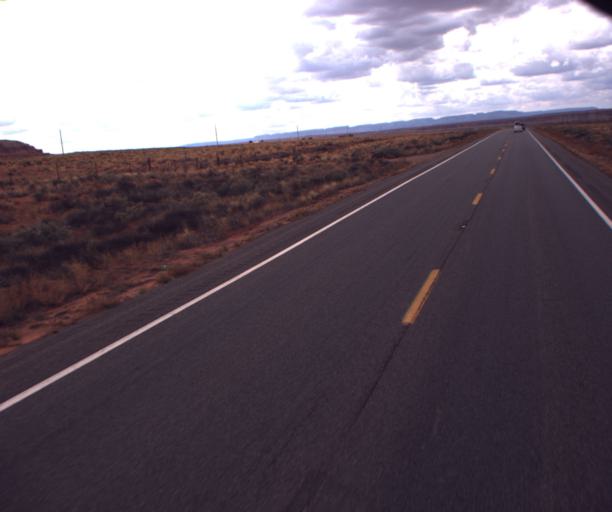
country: US
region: Arizona
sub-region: Navajo County
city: Kayenta
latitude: 36.7952
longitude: -109.9381
